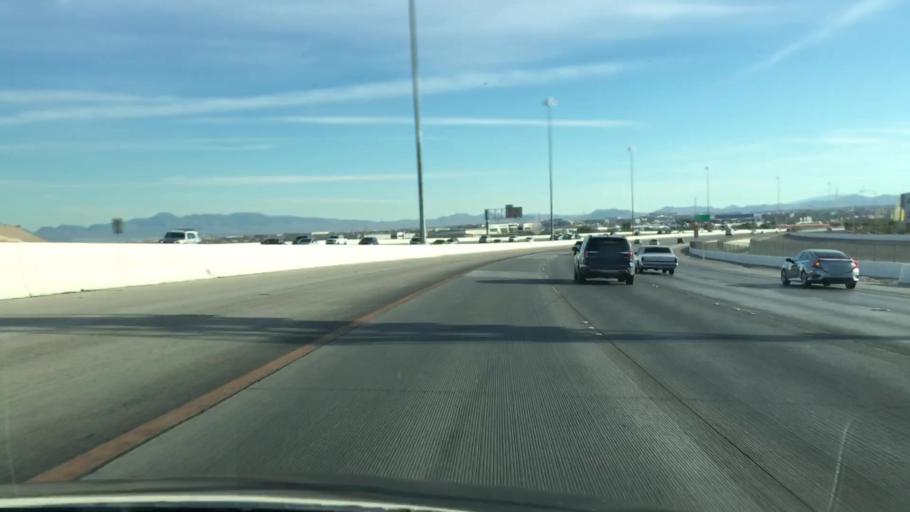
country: US
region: Nevada
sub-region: Clark County
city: Summerlin South
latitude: 36.0955
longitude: -115.2896
